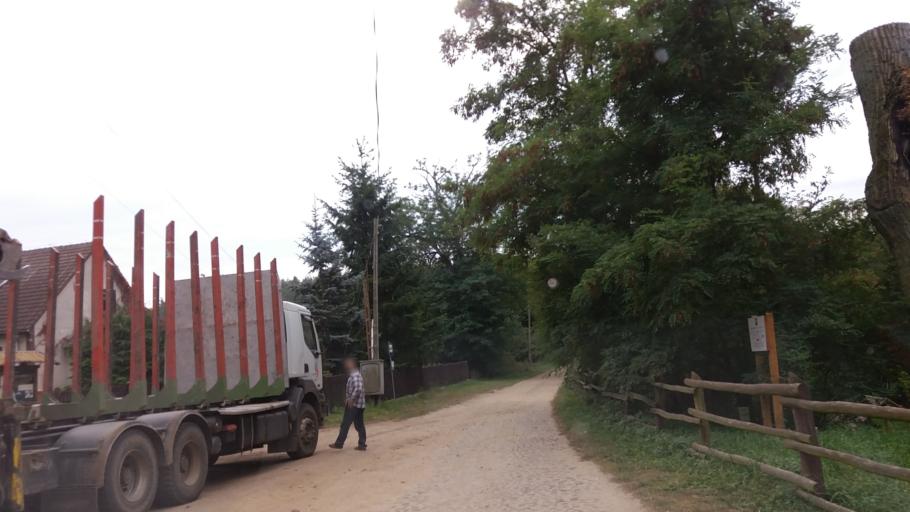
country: PL
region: West Pomeranian Voivodeship
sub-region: Powiat mysliborski
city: Barlinek
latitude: 52.9431
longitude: 15.2525
